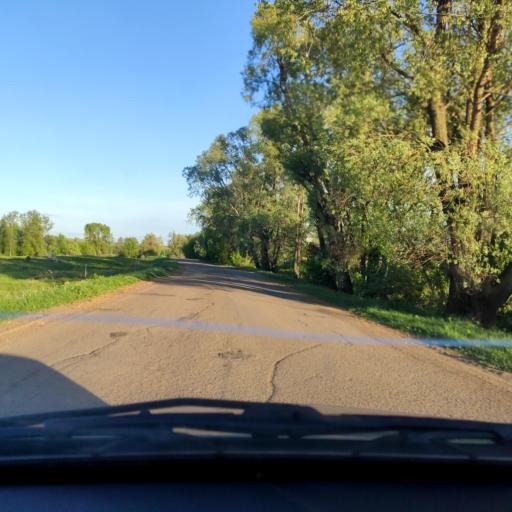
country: RU
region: Bashkortostan
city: Yazykovo
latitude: 55.0394
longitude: 56.1910
